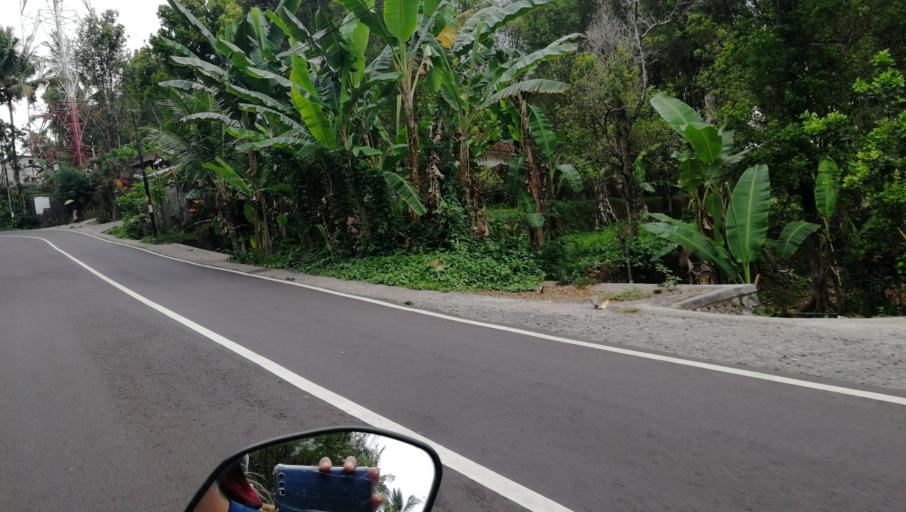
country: ID
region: Bali
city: Banjar Pedawa
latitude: -8.2640
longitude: 115.0378
